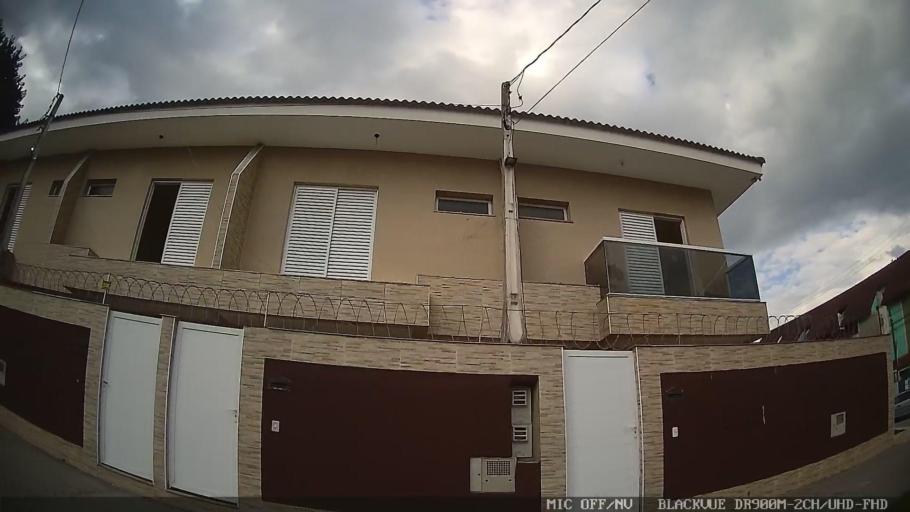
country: BR
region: Sao Paulo
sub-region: Guaruja
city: Guaruja
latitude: -23.9818
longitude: -46.2395
